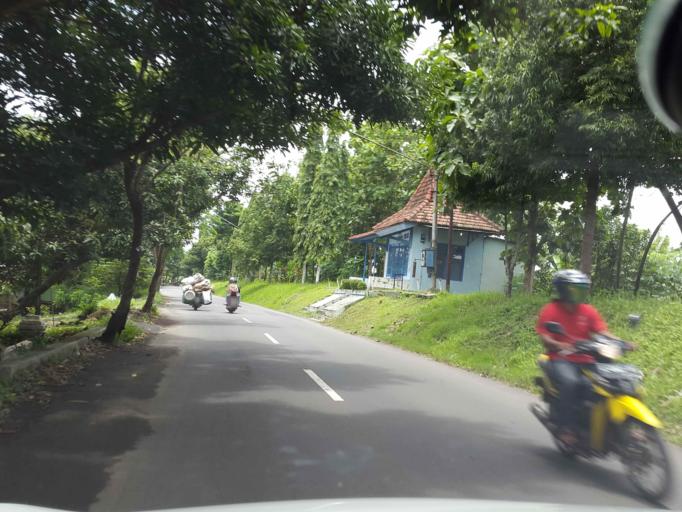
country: ID
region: East Java
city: Mojokerto
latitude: -7.4580
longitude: 112.4184
